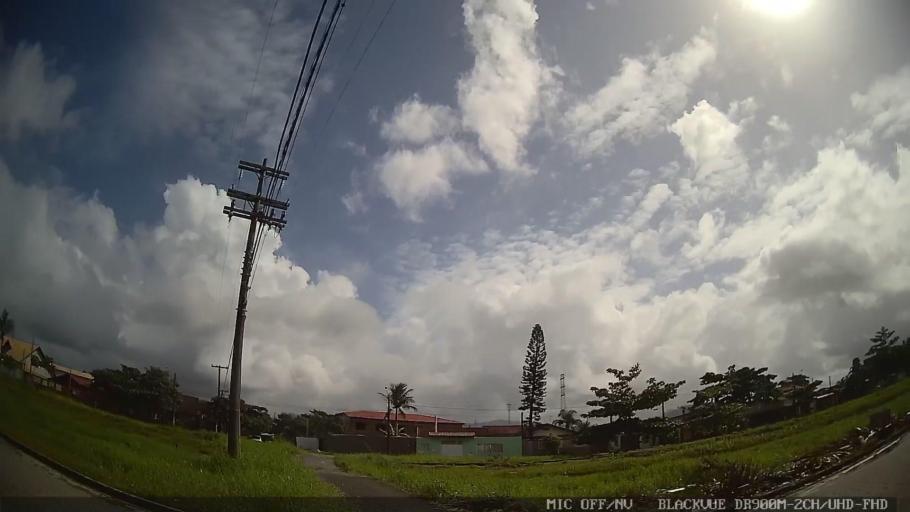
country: BR
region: Sao Paulo
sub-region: Mongagua
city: Mongagua
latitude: -24.1364
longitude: -46.7013
